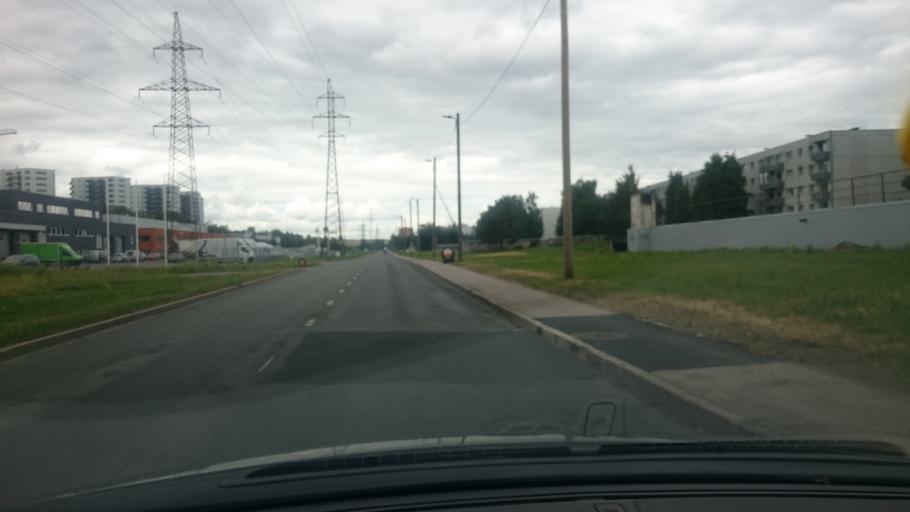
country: EE
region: Harju
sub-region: Saue vald
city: Laagri
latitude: 59.4116
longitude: 24.6557
